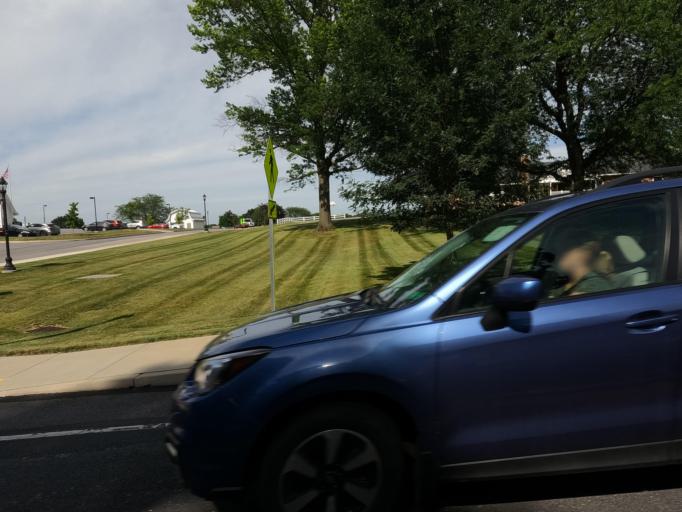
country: US
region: Pennsylvania
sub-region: Dauphin County
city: Palmdale
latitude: 40.2731
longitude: -76.6248
